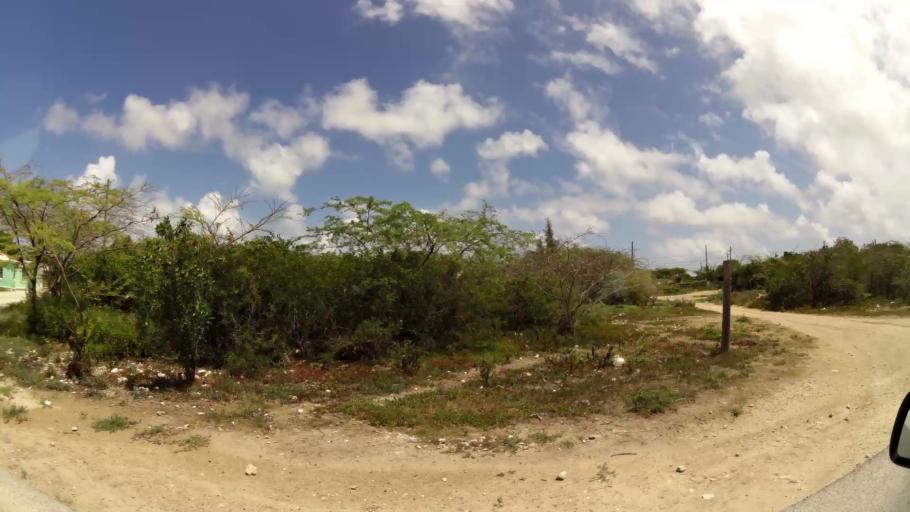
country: TC
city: Cockburn Town
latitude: 21.4583
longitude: -71.1429
